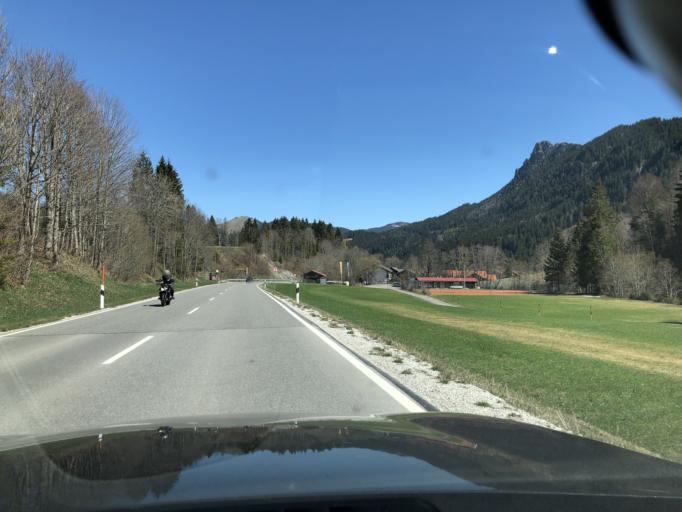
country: AT
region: Tyrol
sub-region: Politischer Bezirk Reutte
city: Schattwald
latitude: 47.5423
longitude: 10.4192
